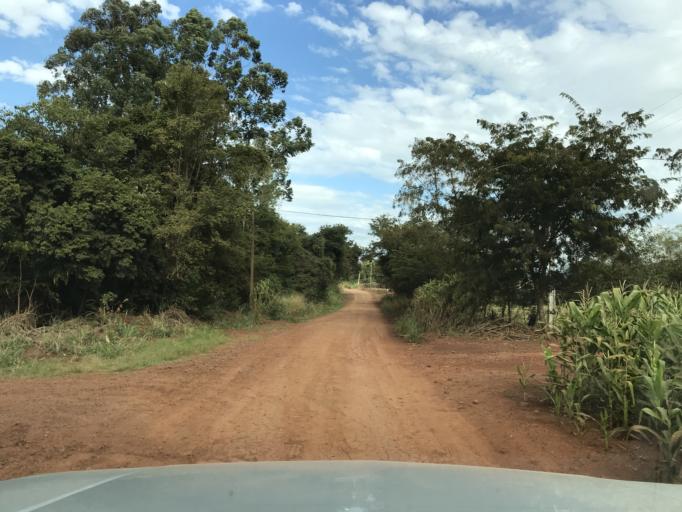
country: BR
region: Parana
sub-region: Palotina
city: Palotina
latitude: -24.3218
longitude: -53.8061
